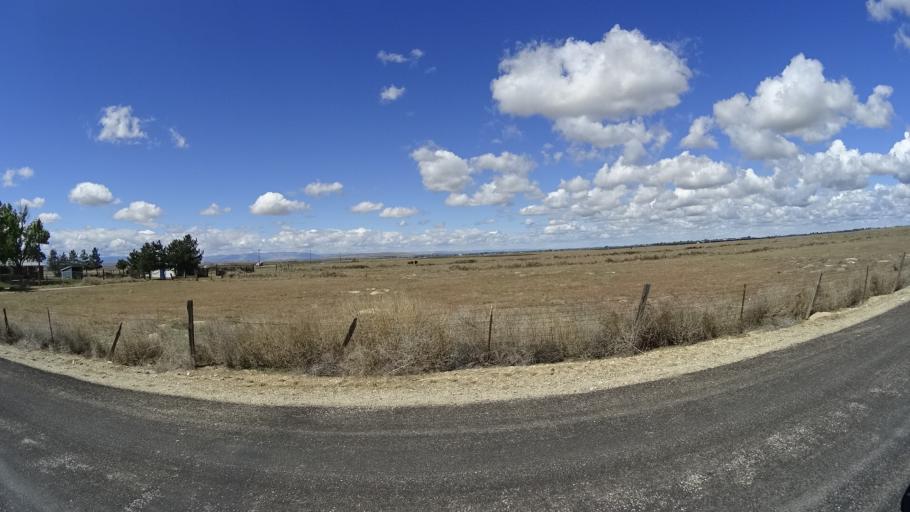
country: US
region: Idaho
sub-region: Ada County
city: Kuna
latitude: 43.4601
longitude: -116.2744
